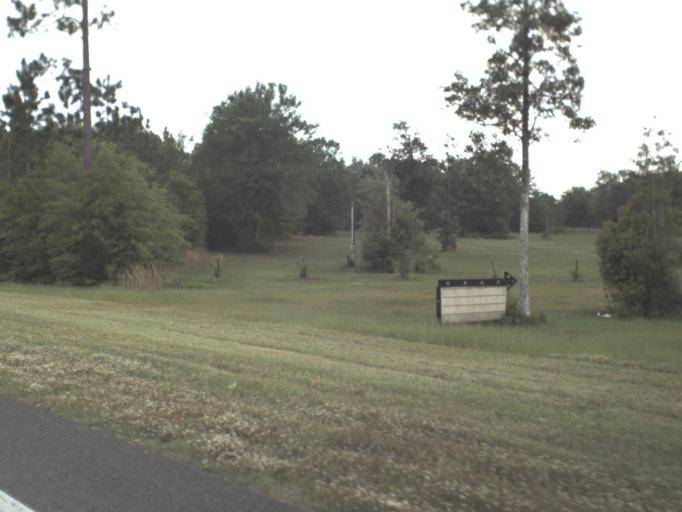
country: US
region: Florida
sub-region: Escambia County
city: Cantonment
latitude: 30.6283
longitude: -87.3315
